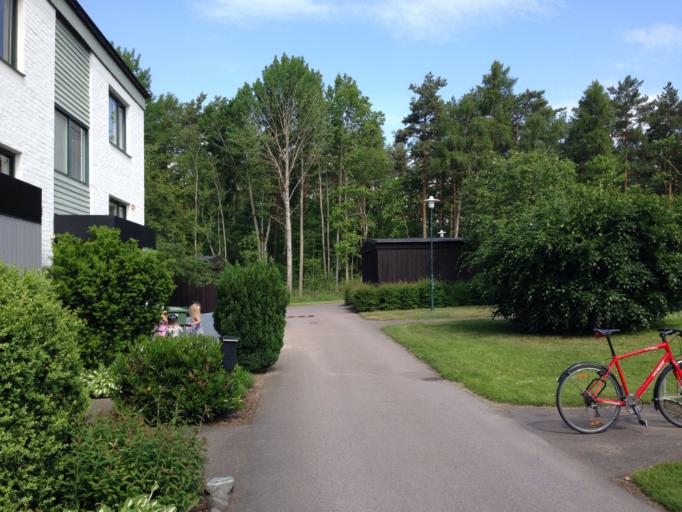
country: SE
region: Kalmar
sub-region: Kalmar Kommun
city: Kalmar
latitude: 56.6544
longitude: 16.3273
